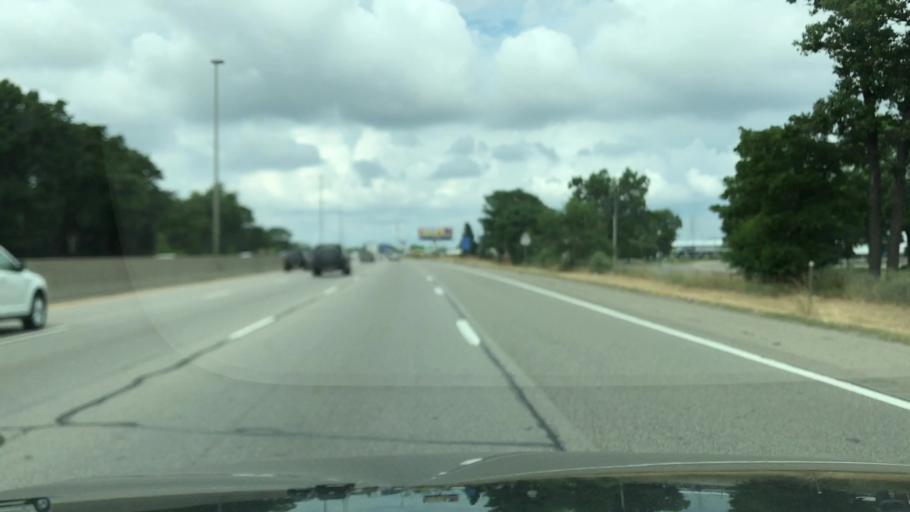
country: US
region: Michigan
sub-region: Kent County
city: Wyoming
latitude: 42.8894
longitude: -85.6791
